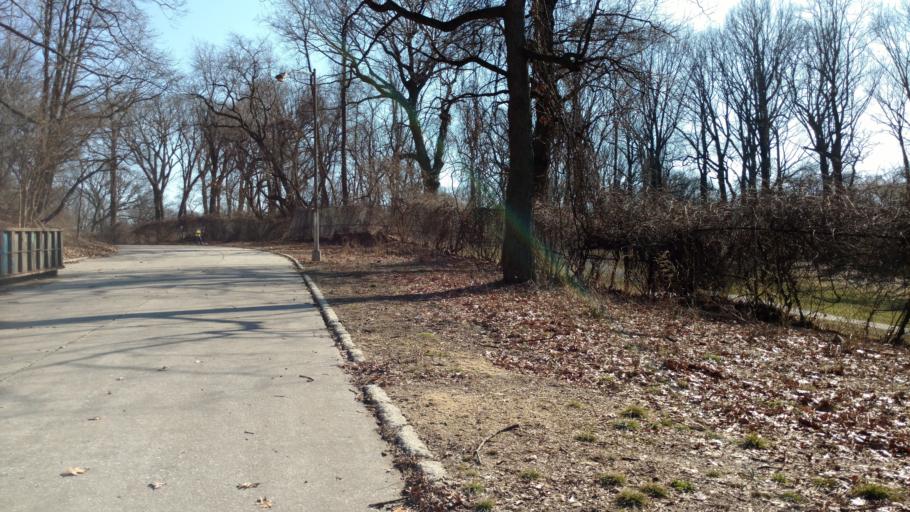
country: US
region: New York
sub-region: Queens County
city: Borough of Queens
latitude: 40.7011
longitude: -73.8610
